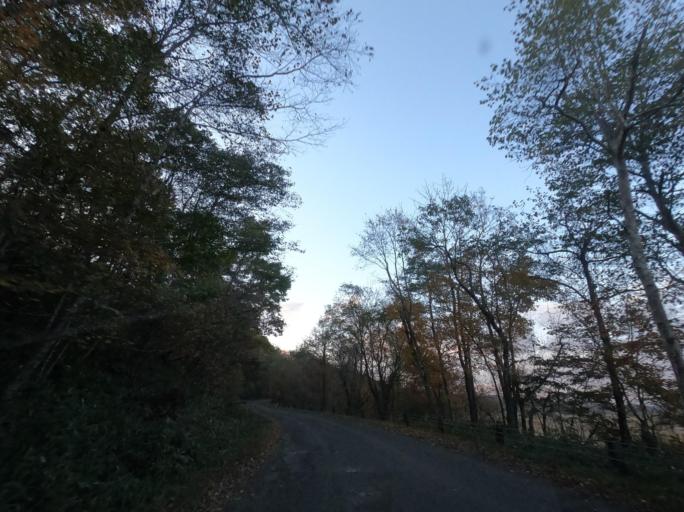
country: JP
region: Hokkaido
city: Kushiro
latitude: 43.1981
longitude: 144.4608
